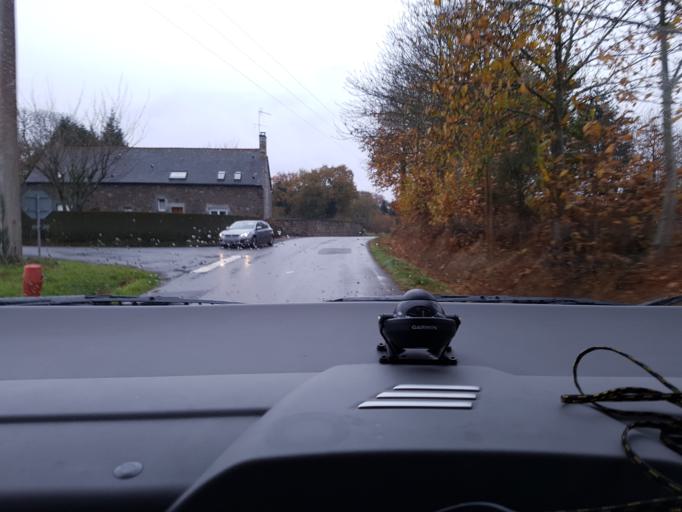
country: FR
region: Brittany
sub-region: Departement d'Ille-et-Vilaine
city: Saint-Brice-en-Cogles
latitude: 48.3972
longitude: -1.3832
